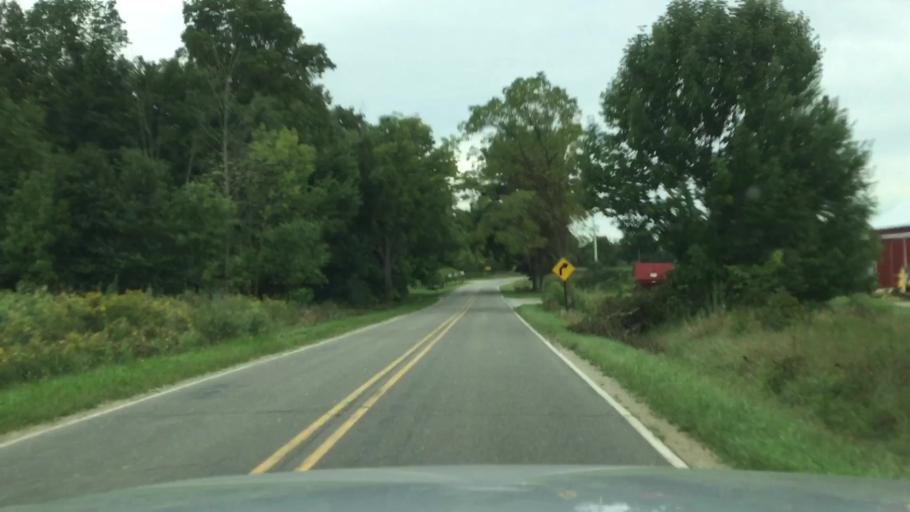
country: US
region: Michigan
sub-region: Shiawassee County
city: Durand
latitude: 42.8453
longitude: -84.0349
